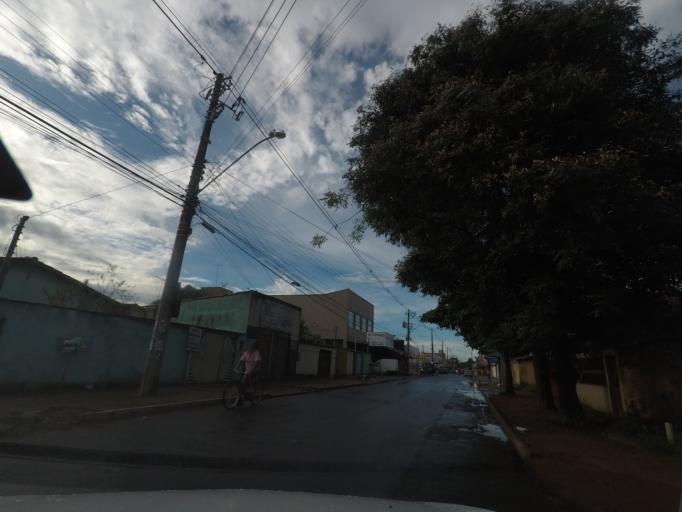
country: BR
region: Goias
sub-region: Aparecida De Goiania
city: Aparecida de Goiania
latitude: -16.7613
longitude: -49.3511
